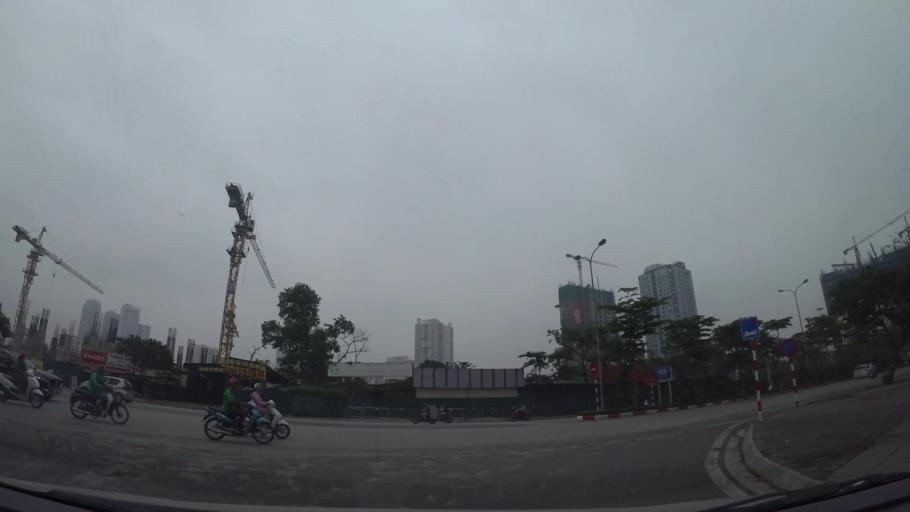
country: VN
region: Ha Noi
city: Cau Giay
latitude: 21.0260
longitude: 105.7881
